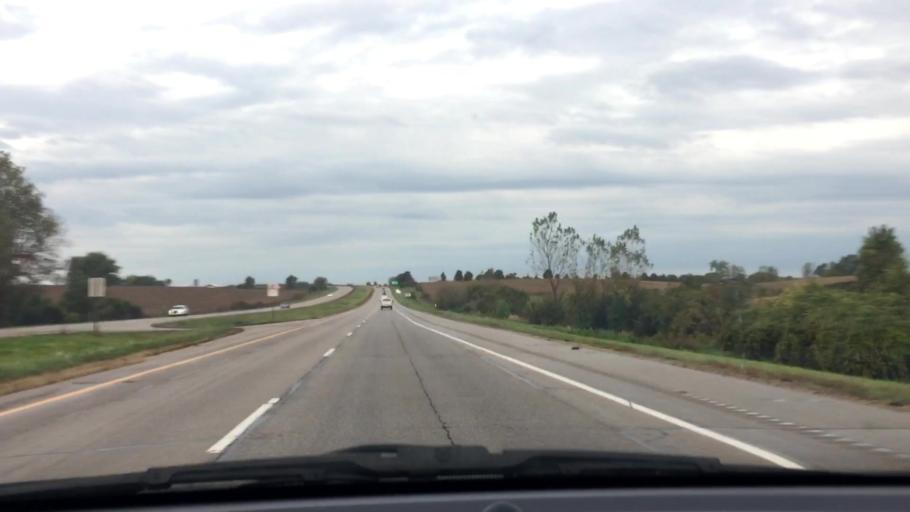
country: US
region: Wisconsin
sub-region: Rock County
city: Clinton
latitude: 42.5729
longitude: -88.8752
